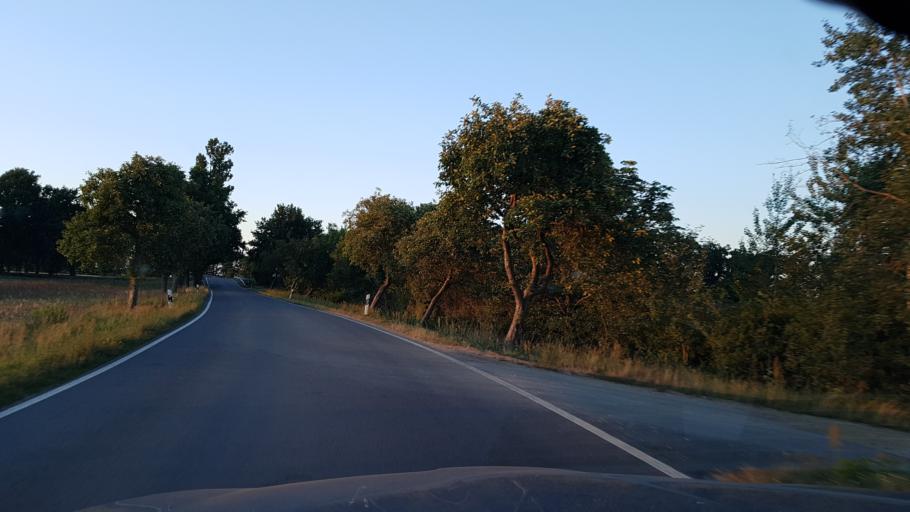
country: DE
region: Brandenburg
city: Groden
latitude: 51.4160
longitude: 13.5958
